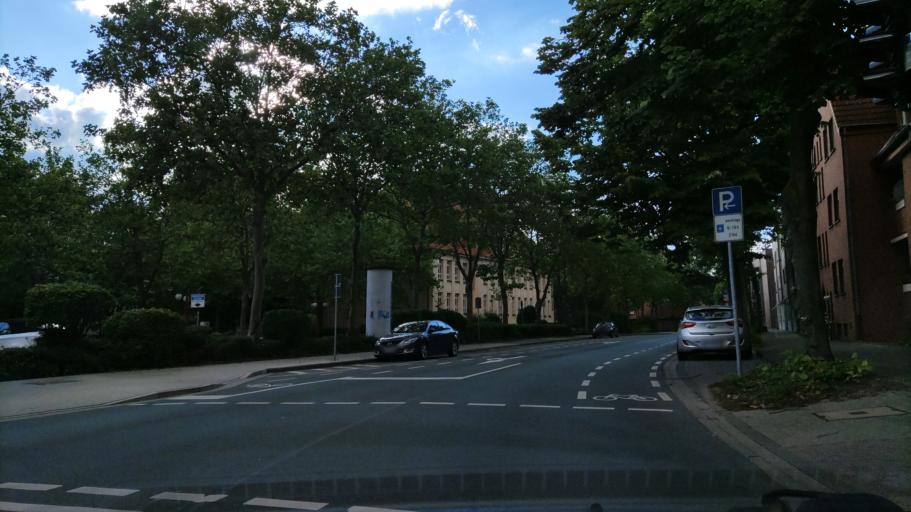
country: DE
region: North Rhine-Westphalia
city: Ahlen
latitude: 51.7610
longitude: 7.8888
